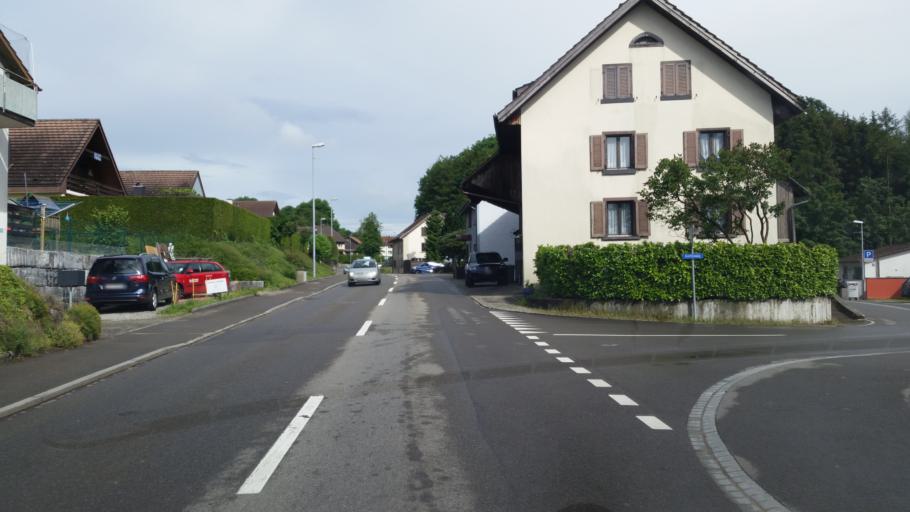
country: CH
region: Aargau
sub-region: Bezirk Muri
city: Waltenschwil
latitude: 47.3346
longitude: 8.3056
